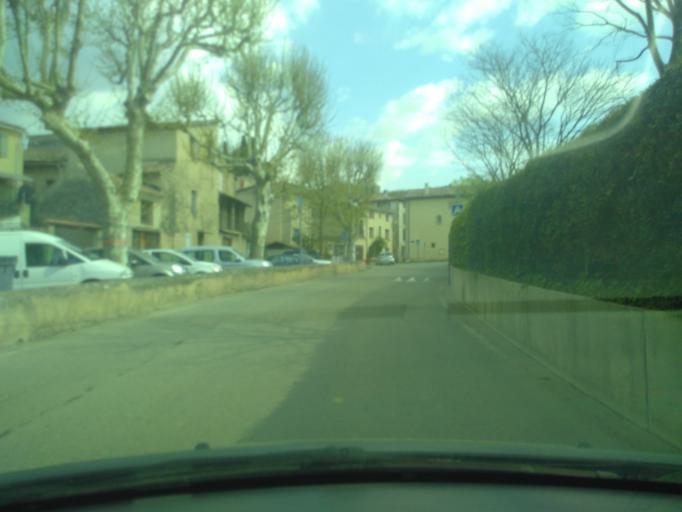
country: FR
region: Provence-Alpes-Cote d'Azur
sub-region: Departement du Vaucluse
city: Malaucene
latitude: 44.1741
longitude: 5.1302
